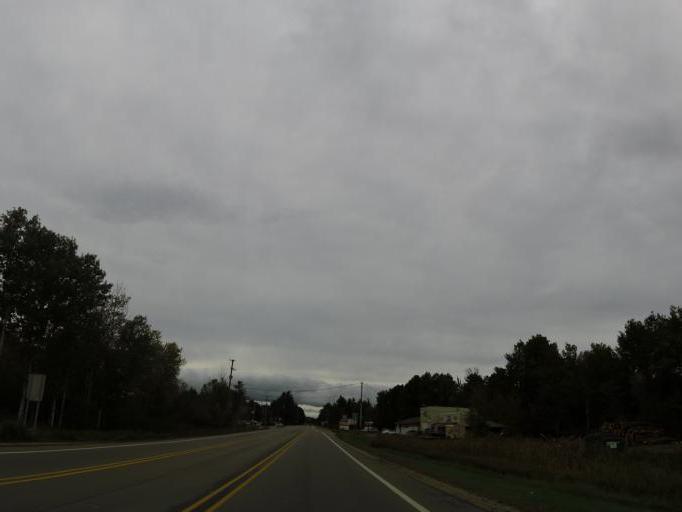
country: US
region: Michigan
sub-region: Roscommon County
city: Roscommon
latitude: 44.5028
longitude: -84.5997
